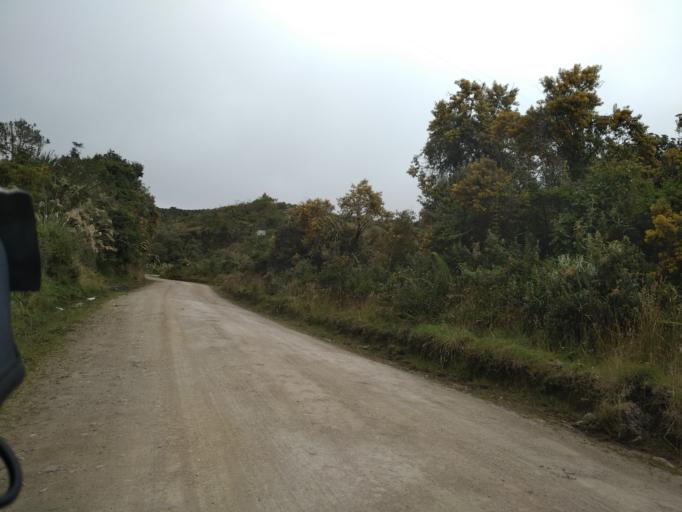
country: EC
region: Carchi
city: Tulcan
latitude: 0.7403
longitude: -77.7854
